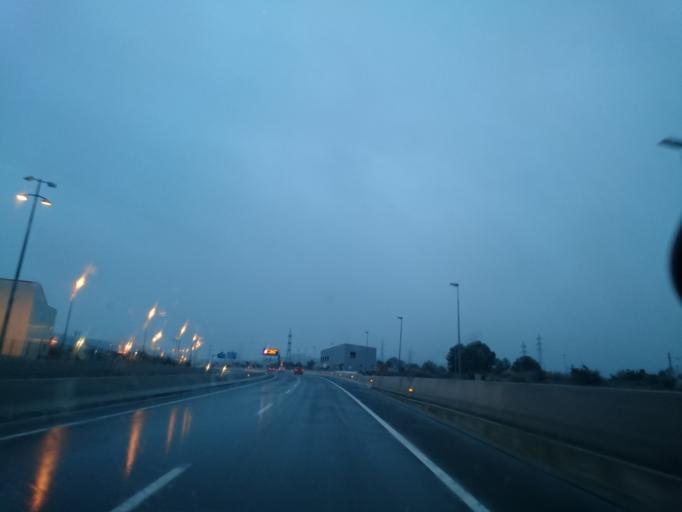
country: ES
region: Catalonia
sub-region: Provincia de Barcelona
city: Vilanova i la Geltru
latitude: 41.2482
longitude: 1.7199
